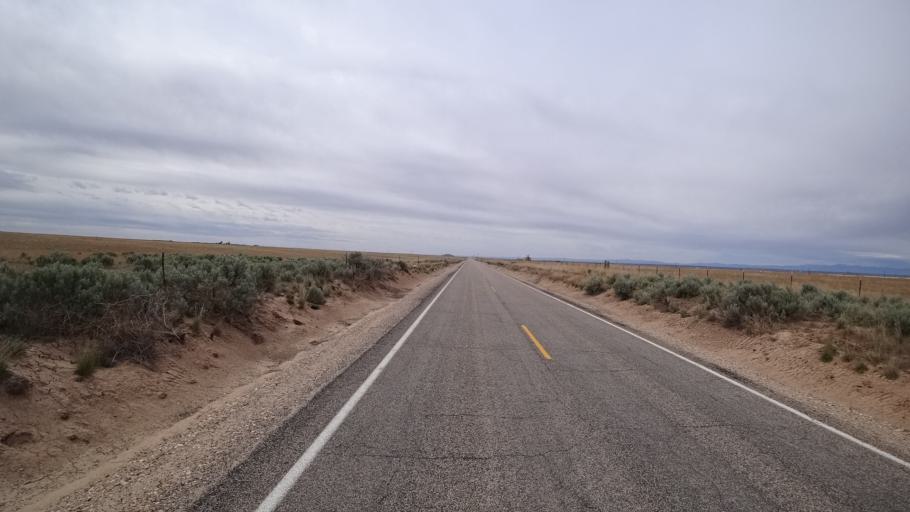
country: US
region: Idaho
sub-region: Ada County
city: Boise
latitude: 43.3565
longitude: -116.0049
